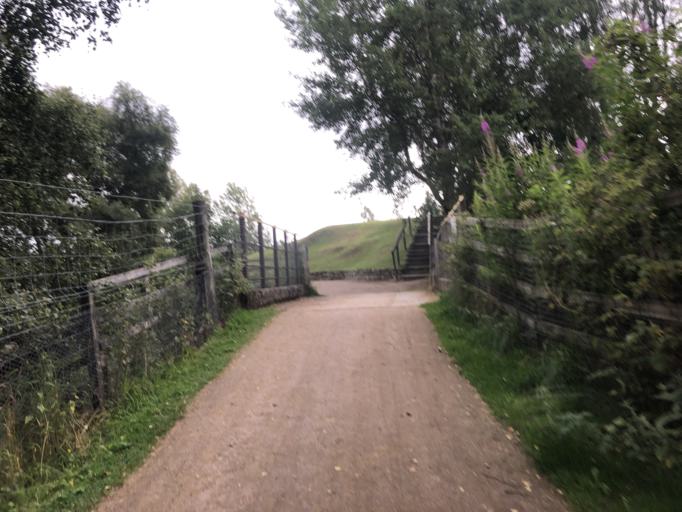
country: GB
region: Scotland
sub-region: Highland
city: Kingussie
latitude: 57.0650
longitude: -4.1104
